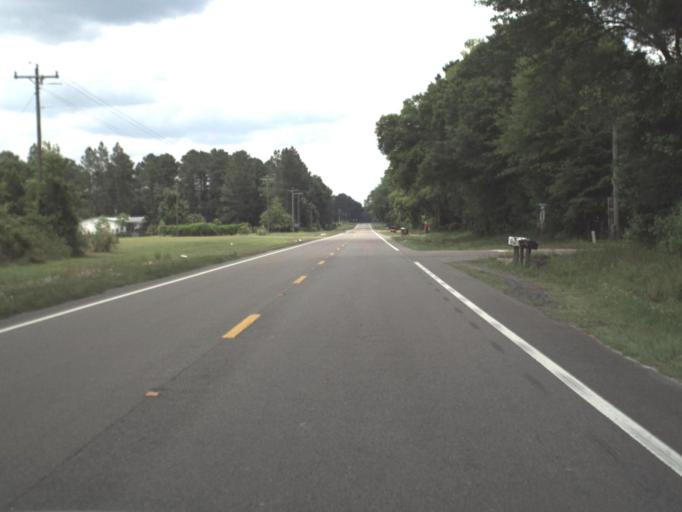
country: US
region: Florida
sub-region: Columbia County
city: Five Points
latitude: 30.3088
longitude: -82.6307
